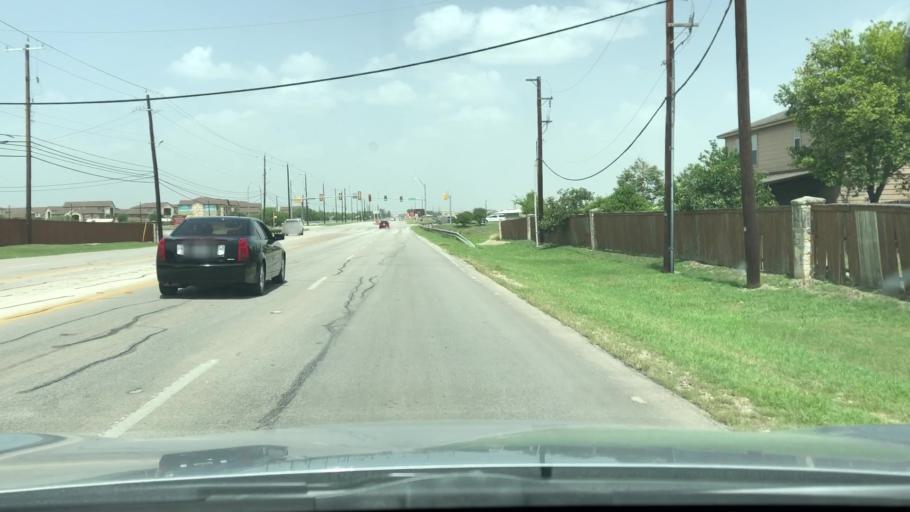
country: US
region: Texas
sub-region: Bexar County
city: Selma
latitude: 29.5867
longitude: -98.3266
